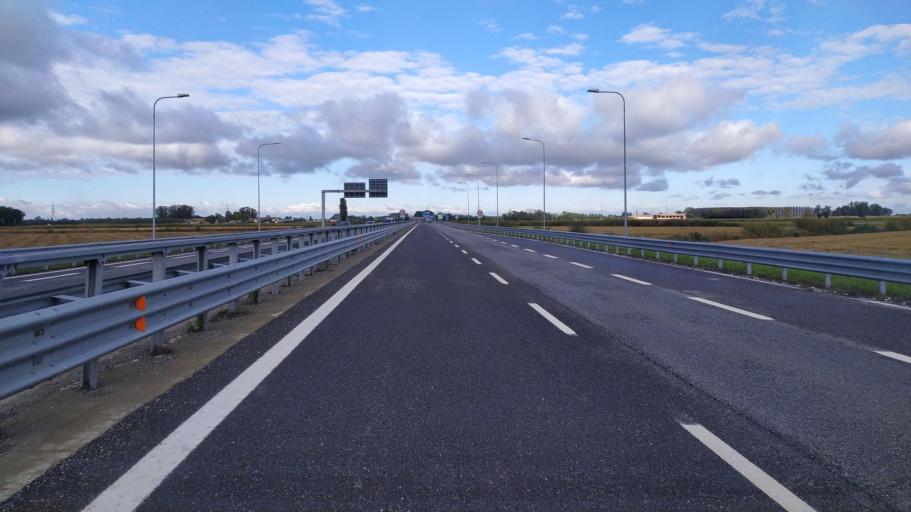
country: IT
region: Lombardy
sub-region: Provincia di Pavia
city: Torre d'Isola
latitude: 45.2358
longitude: 9.0648
